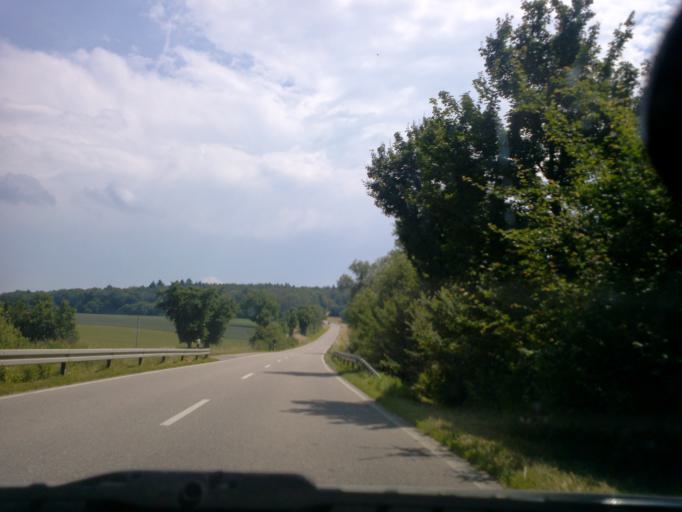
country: DE
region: Baden-Wuerttemberg
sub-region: Karlsruhe Region
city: Woessingen
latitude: 49.0068
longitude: 8.6281
